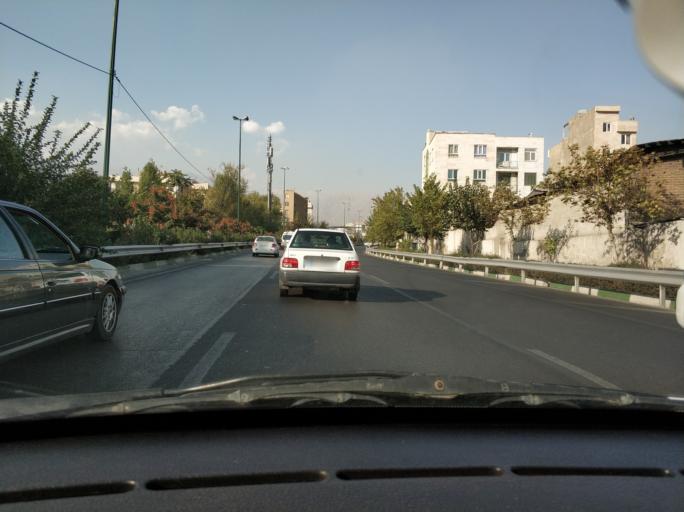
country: IR
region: Tehran
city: Tehran
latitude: 35.7465
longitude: 51.4641
